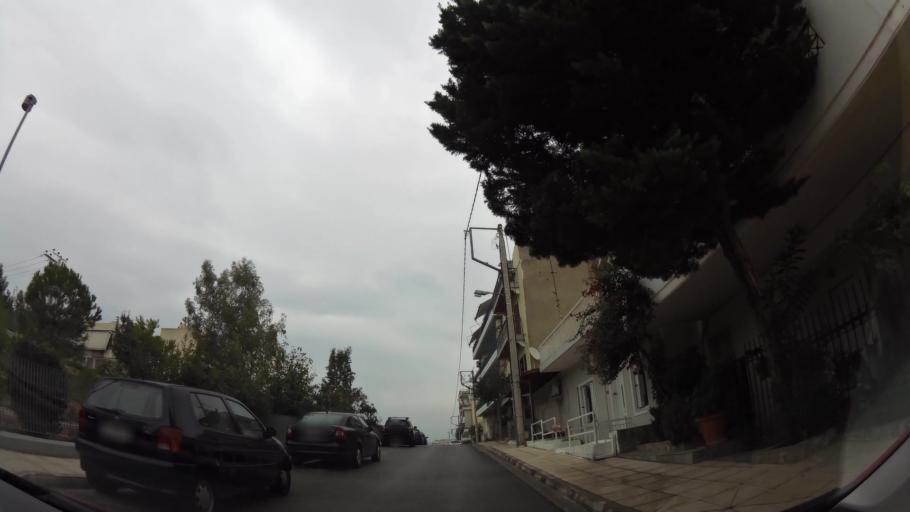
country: GR
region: Attica
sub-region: Nomarchia Athinas
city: Agioi Anargyroi
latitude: 38.0377
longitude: 23.7268
